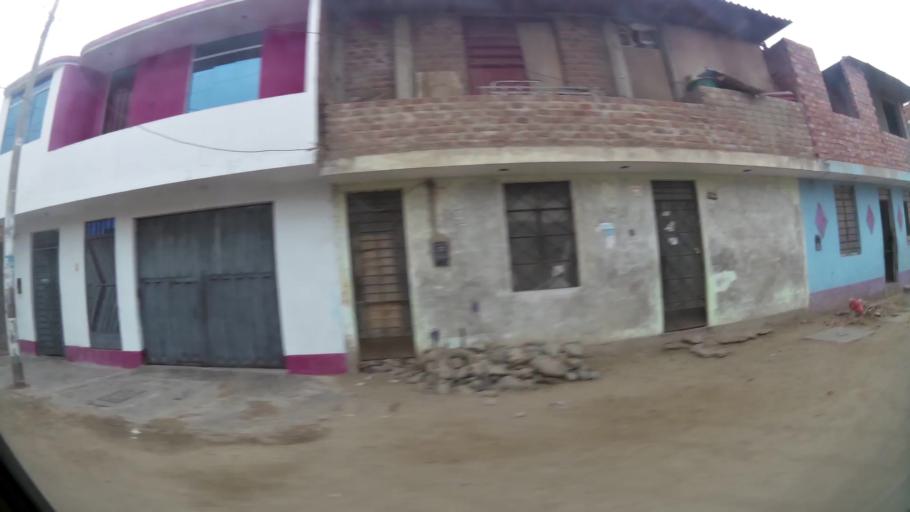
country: PE
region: La Libertad
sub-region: Provincia de Trujillo
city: La Esperanza
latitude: -8.0671
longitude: -79.0199
